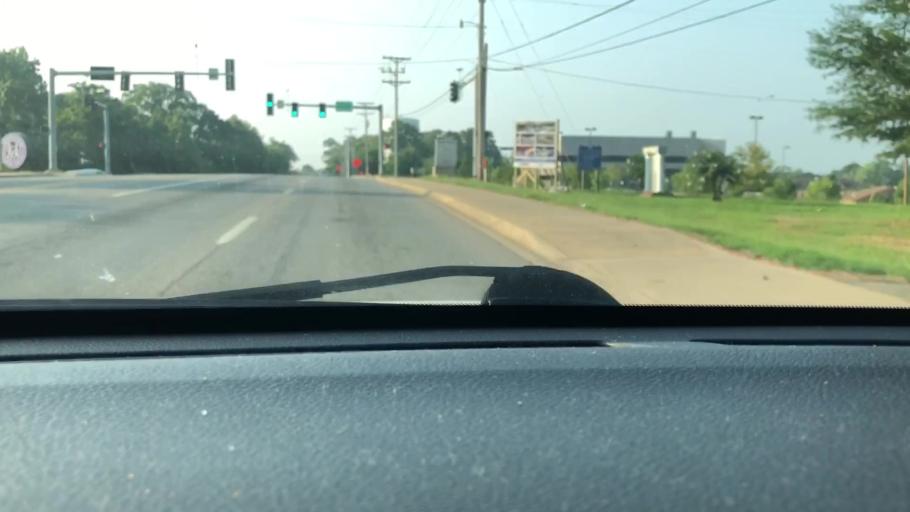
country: US
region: Arkansas
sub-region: Saline County
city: Bryant
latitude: 34.6033
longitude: -92.4909
